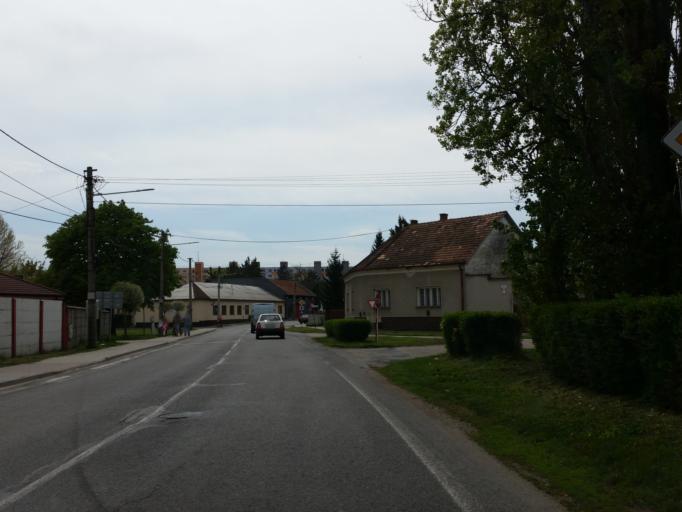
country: SK
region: Trnavsky
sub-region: Okres Dunajska Streda
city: Velky Meder
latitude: 47.8580
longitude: 17.7756
